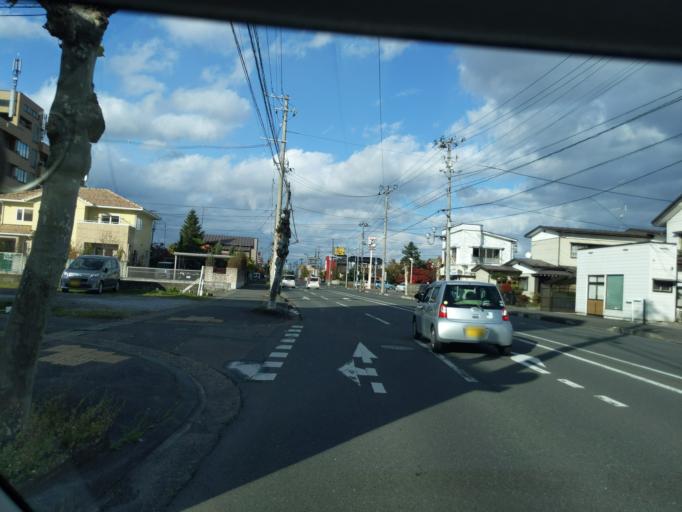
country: JP
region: Iwate
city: Mizusawa
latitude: 39.1346
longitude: 141.1552
